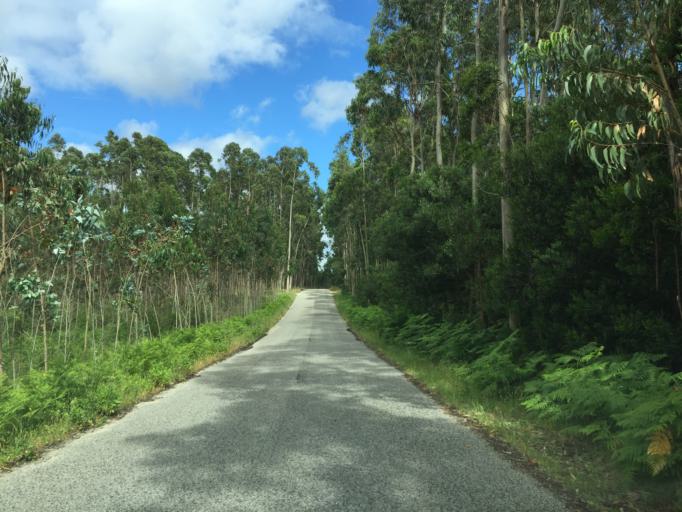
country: PT
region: Coimbra
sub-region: Figueira da Foz
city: Tavarede
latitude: 40.2108
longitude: -8.8338
